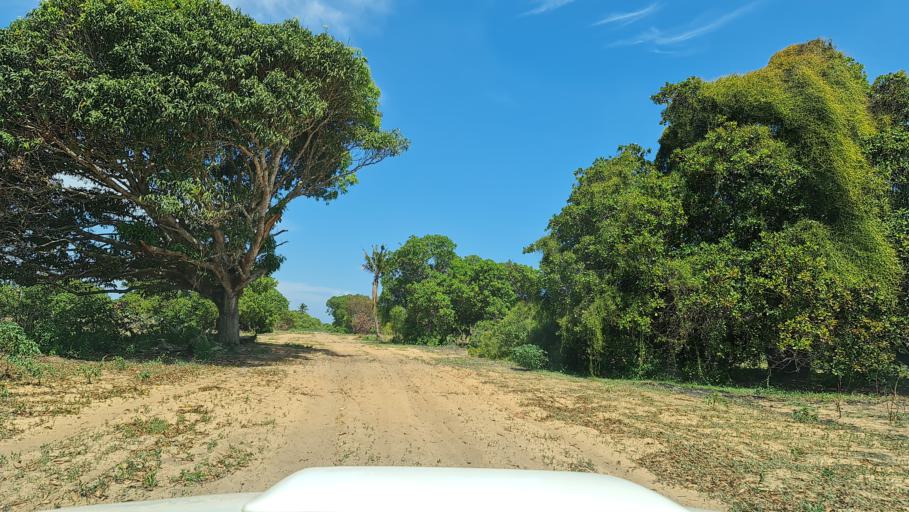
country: MZ
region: Nampula
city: Ilha de Mocambique
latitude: -15.1985
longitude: 40.6097
